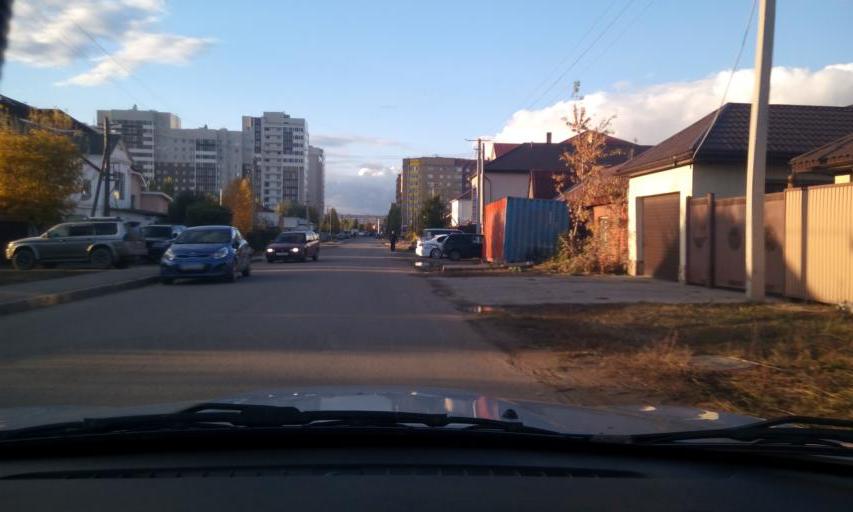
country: KZ
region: Astana Qalasy
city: Astana
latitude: 51.1382
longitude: 71.4872
